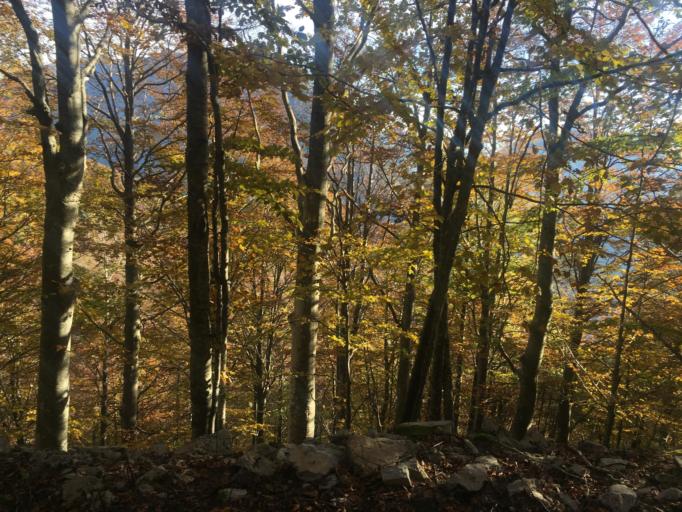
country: IT
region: Friuli Venezia Giulia
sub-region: Provincia di Udine
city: Preone
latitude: 46.3427
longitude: 12.8614
